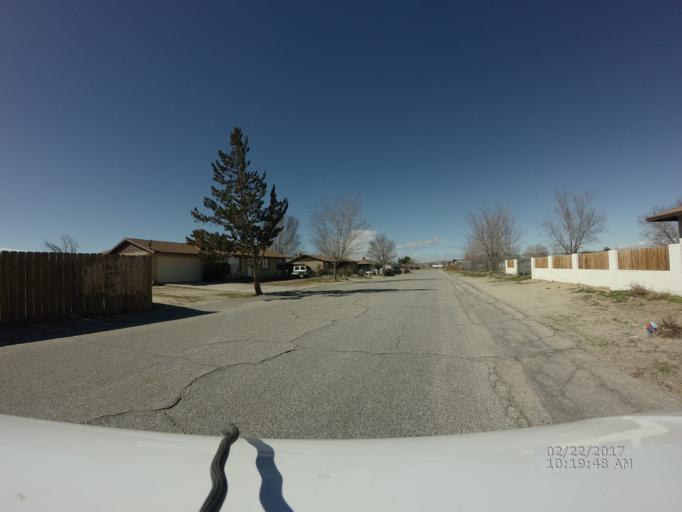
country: US
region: California
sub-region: Los Angeles County
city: Lake Los Angeles
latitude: 34.6248
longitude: -117.8327
